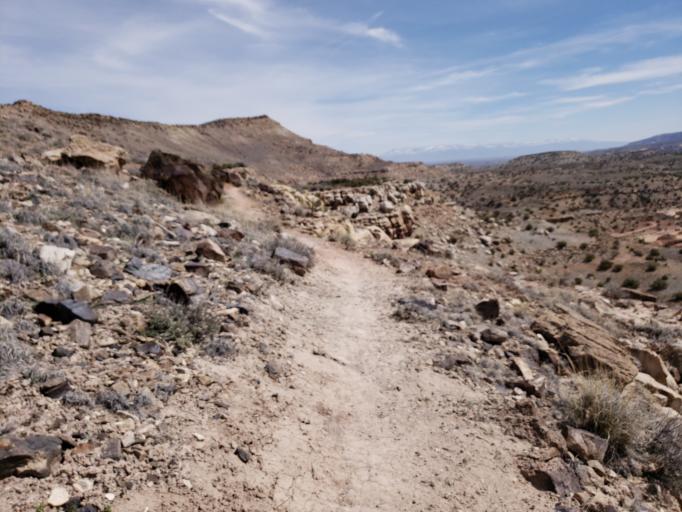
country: US
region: Colorado
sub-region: Mesa County
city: Loma
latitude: 39.1835
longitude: -108.8639
